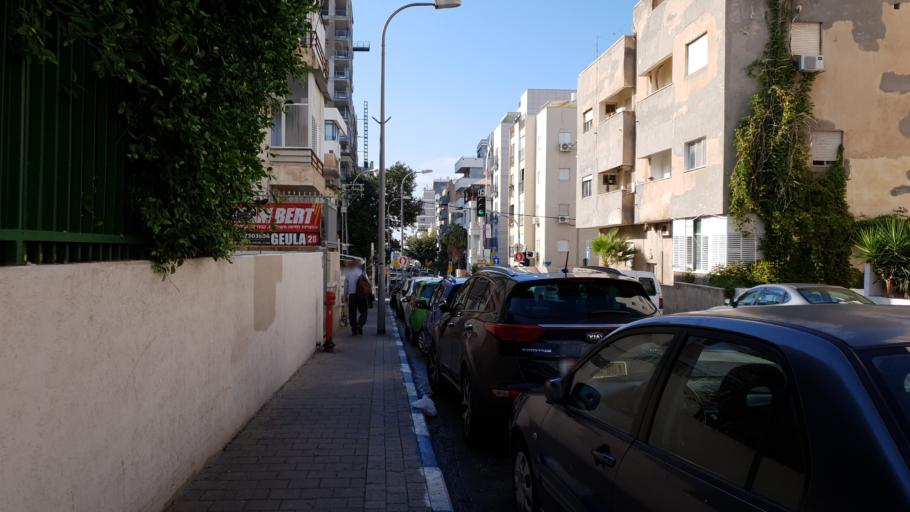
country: IL
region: Tel Aviv
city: Tel Aviv
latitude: 32.0716
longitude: 34.7679
